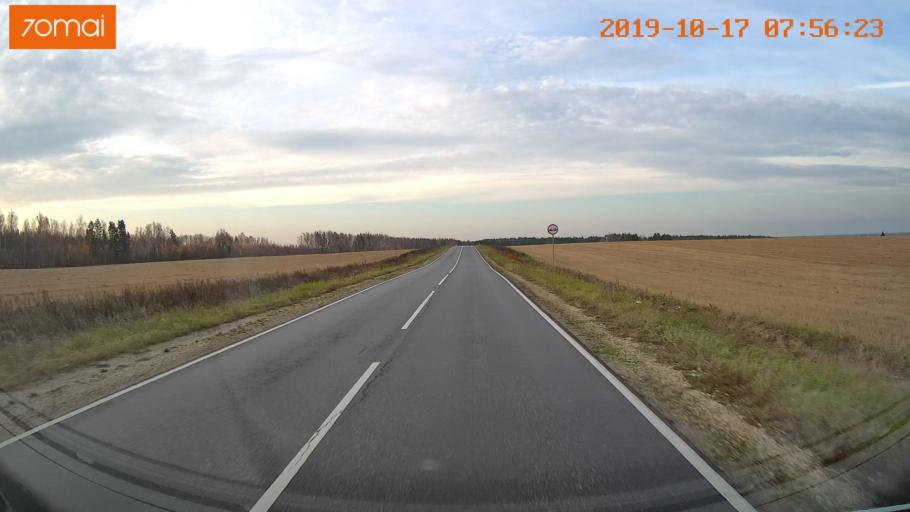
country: RU
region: Vladimir
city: Bavleny
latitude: 56.4239
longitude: 39.5913
